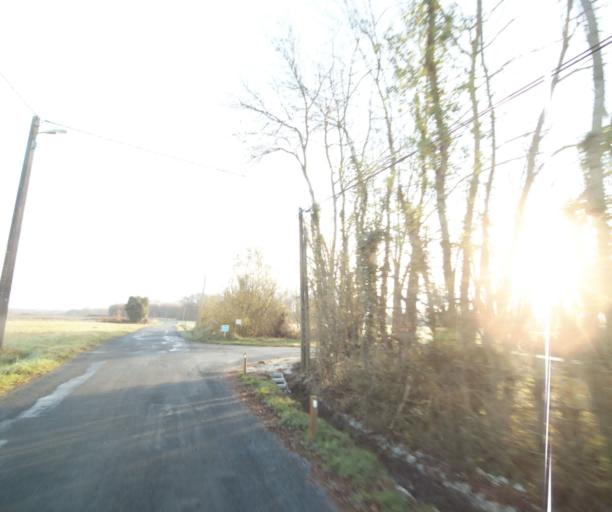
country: FR
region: Poitou-Charentes
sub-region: Departement de la Charente-Maritime
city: Fontcouverte
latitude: 45.7702
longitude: -0.5760
